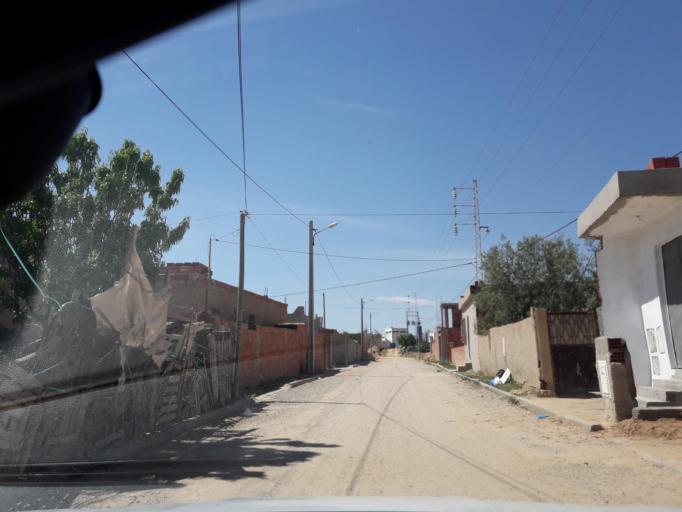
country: TN
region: Safaqis
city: Sfax
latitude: 34.7461
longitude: 10.5119
